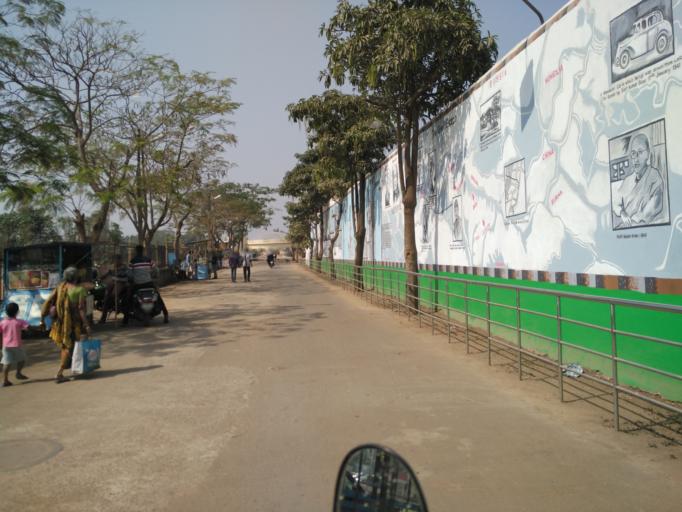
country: IN
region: Odisha
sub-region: Cuttack
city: Cuttack
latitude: 20.4688
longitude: 85.8696
